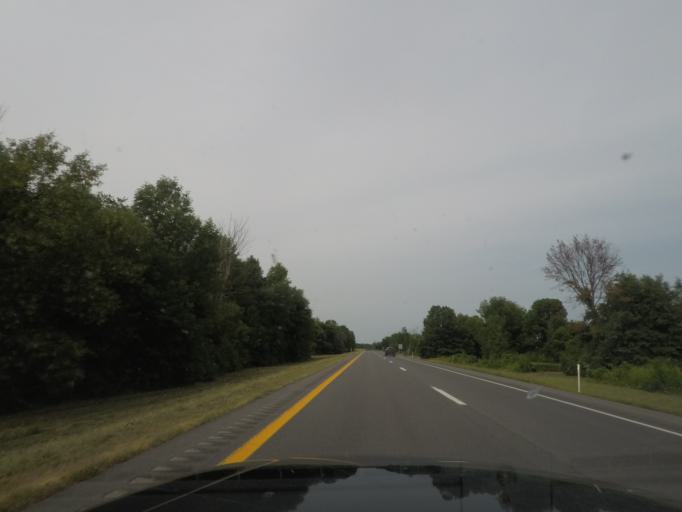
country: US
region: New York
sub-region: Clinton County
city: Cumberland Head
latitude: 44.7385
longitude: -73.4323
